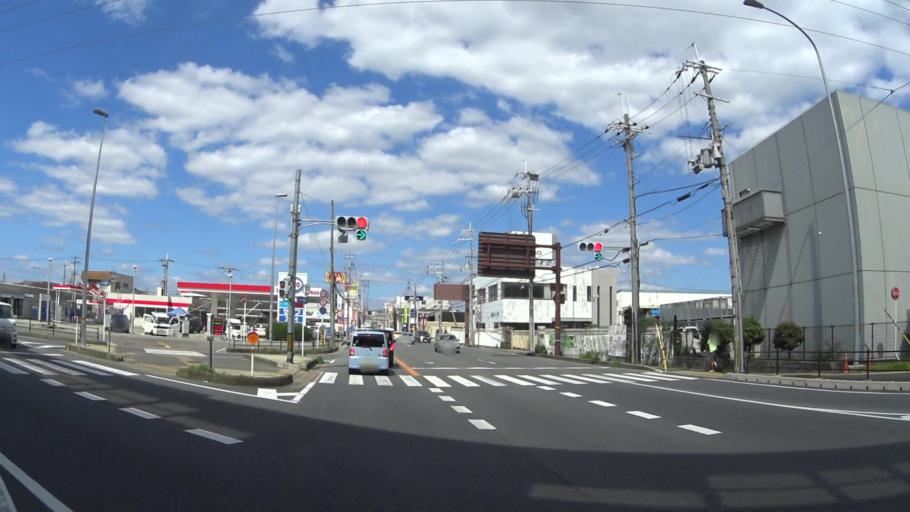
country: JP
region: Kyoto
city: Uji
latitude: 34.9084
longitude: 135.7838
